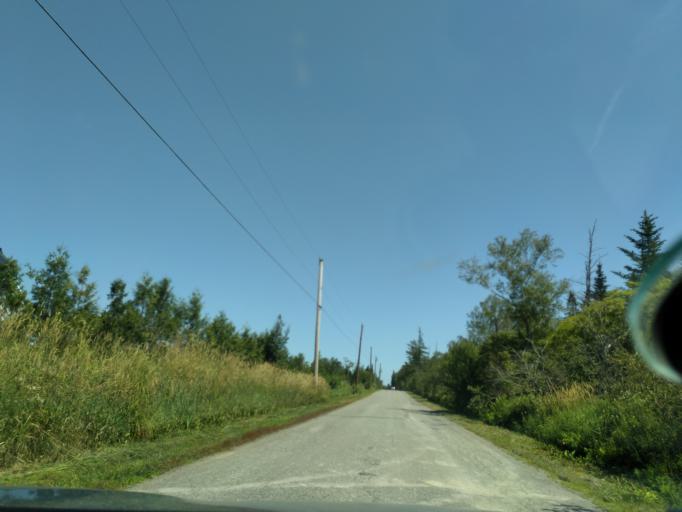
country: US
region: Maine
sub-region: Washington County
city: Eastport
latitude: 44.8311
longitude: -66.9982
